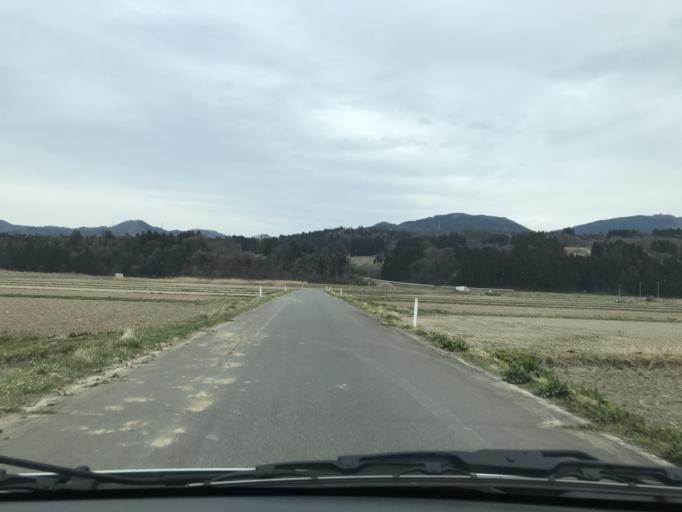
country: JP
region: Iwate
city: Mizusawa
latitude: 39.0539
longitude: 141.1639
